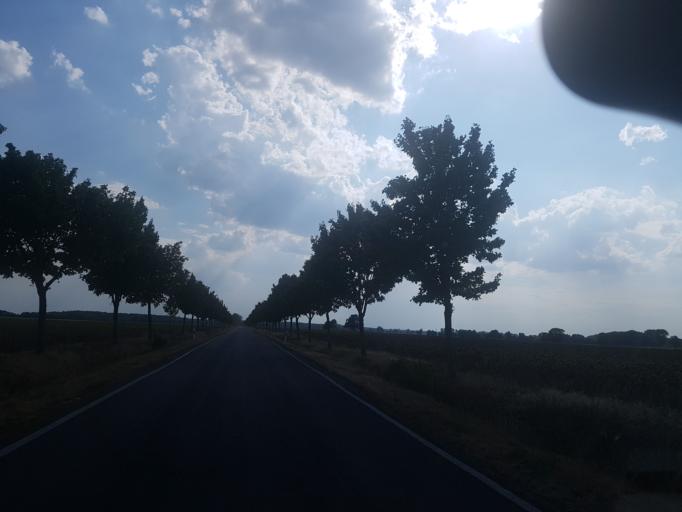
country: DE
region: Saxony-Anhalt
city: Holzdorf
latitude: 51.8074
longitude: 13.2291
